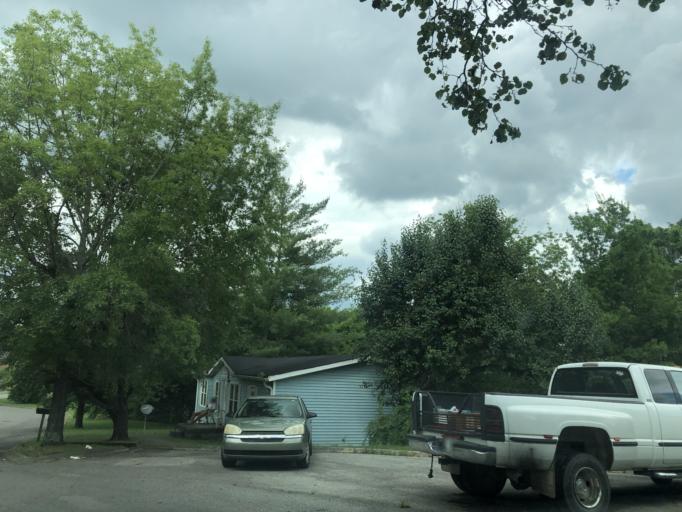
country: US
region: Tennessee
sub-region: Davidson County
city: Nashville
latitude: 36.2208
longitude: -86.7643
